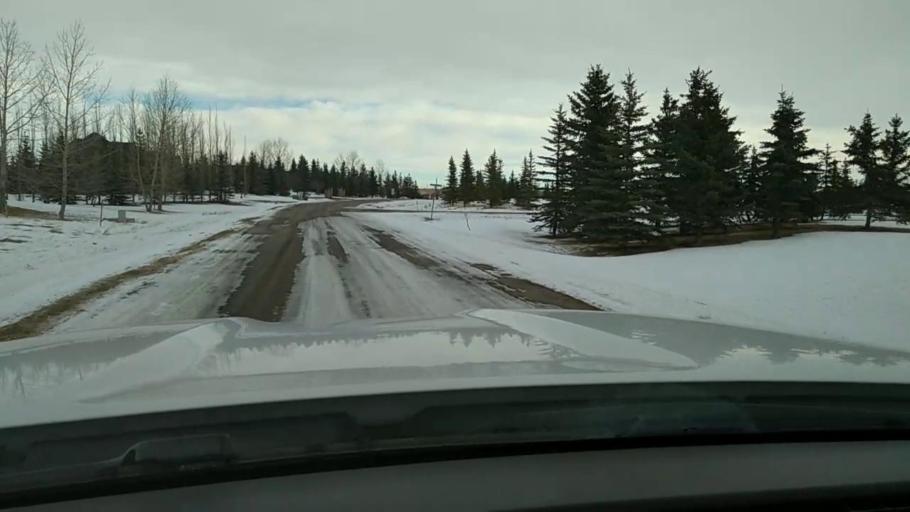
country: CA
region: Alberta
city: Cochrane
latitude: 51.2046
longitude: -114.2845
